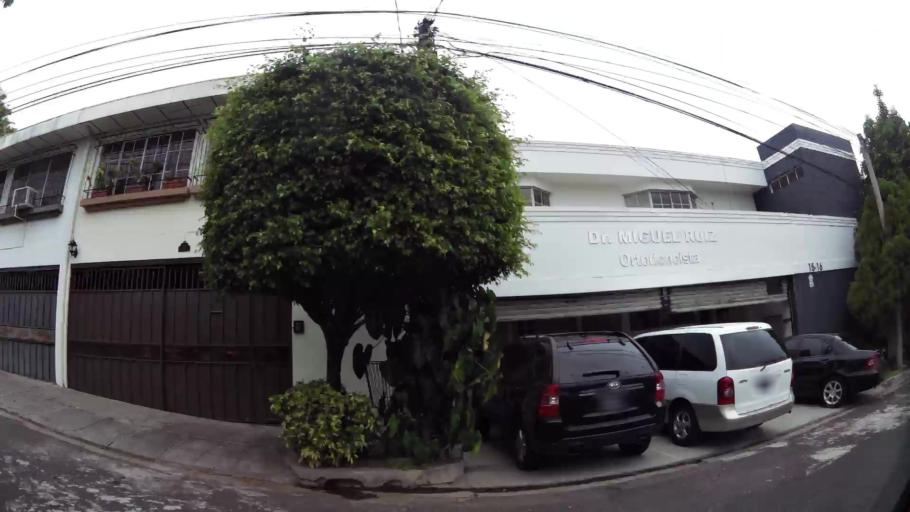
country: SV
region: La Libertad
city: Antiguo Cuscatlan
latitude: 13.7040
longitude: -89.2413
